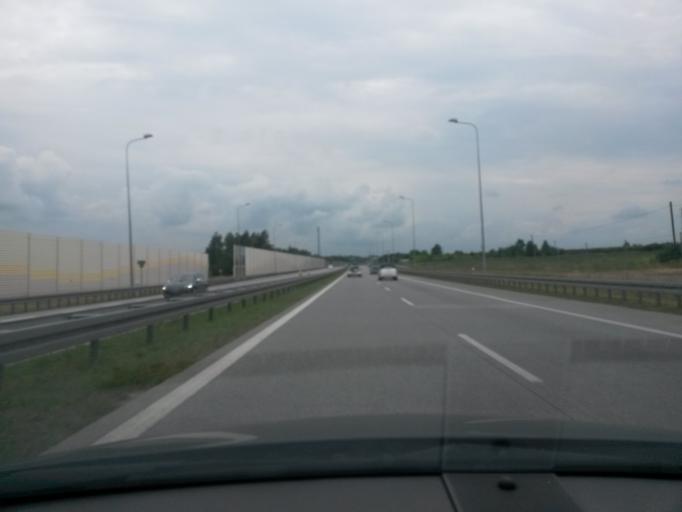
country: PL
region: Lodz Voivodeship
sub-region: Powiat skierniewicki
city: Kowiesy
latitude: 51.8949
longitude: 20.4261
